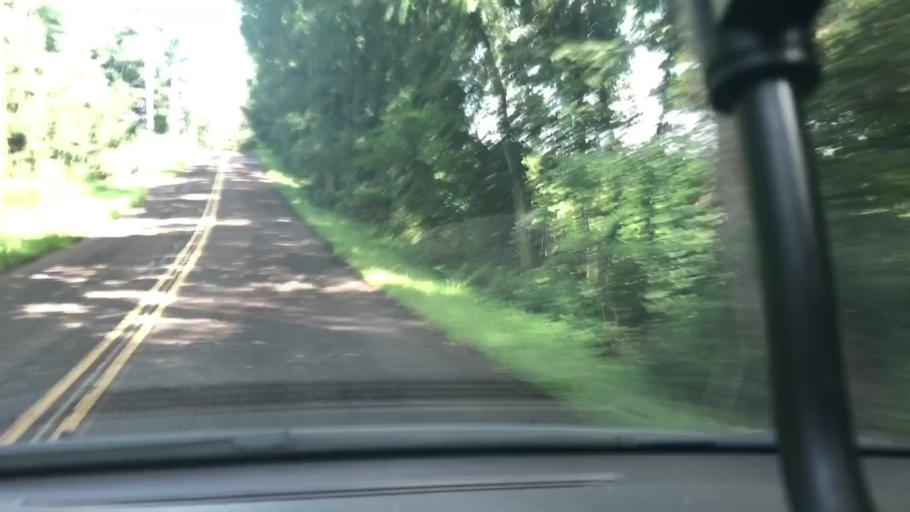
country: US
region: Pennsylvania
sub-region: Chester County
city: Kenilworth
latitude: 40.1858
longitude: -75.6514
